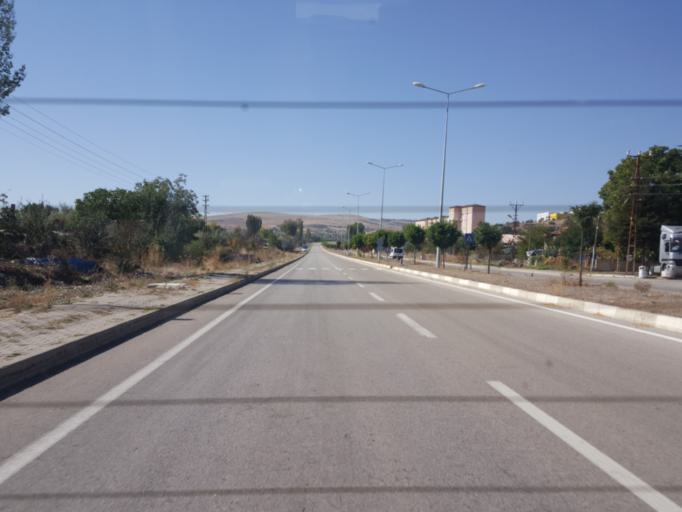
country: TR
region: Tokat
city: Zile
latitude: 40.2865
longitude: 35.8633
